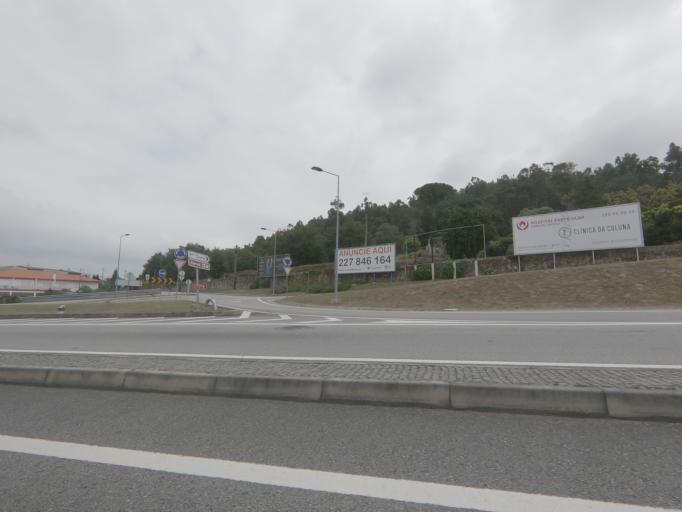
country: PT
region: Viana do Castelo
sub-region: Vila Nova de Cerveira
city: Vila Nova de Cerveira
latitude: 41.9465
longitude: -8.7405
